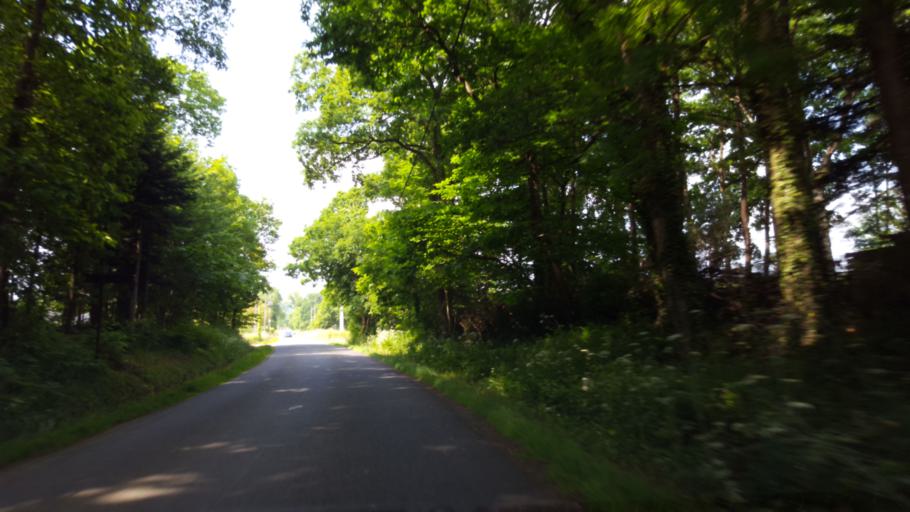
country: FR
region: Brittany
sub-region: Departement d'Ille-et-Vilaine
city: Guignen
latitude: 47.9275
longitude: -1.9058
